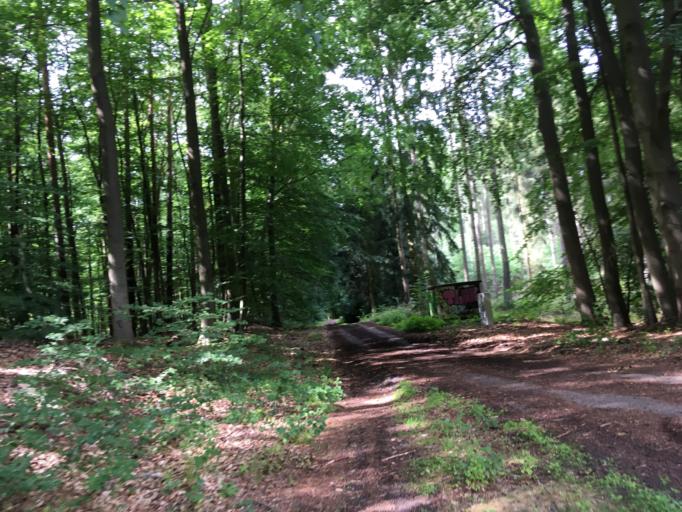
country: DE
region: Brandenburg
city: Bernau bei Berlin
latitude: 52.7452
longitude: 13.5406
